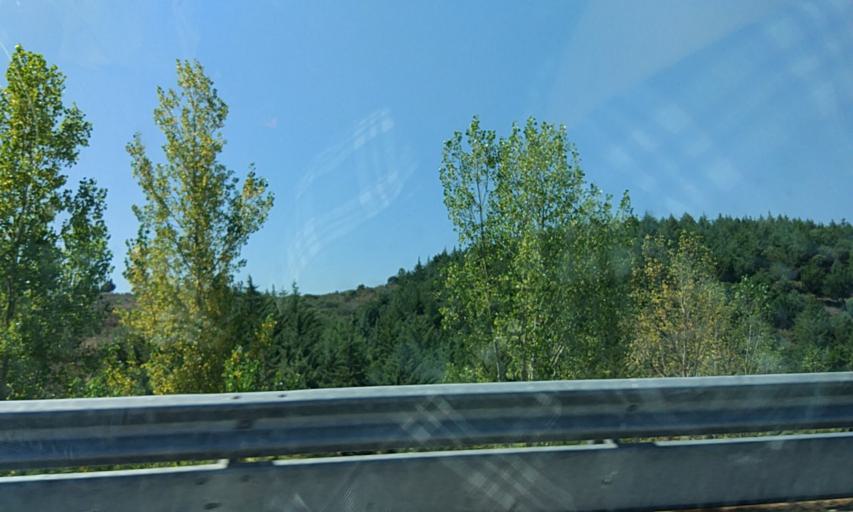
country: PT
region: Braganca
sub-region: Mirandela
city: Mirandela
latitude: 41.5188
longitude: -7.1345
